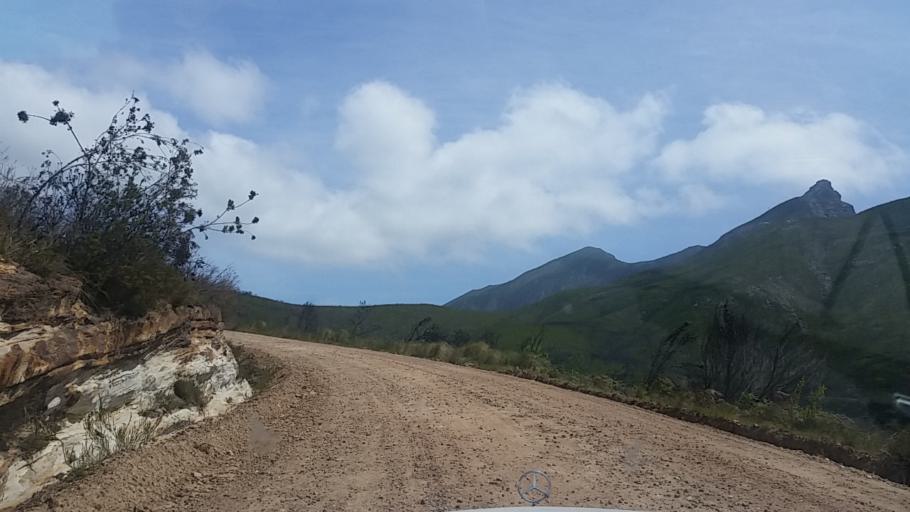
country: ZA
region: Western Cape
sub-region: Eden District Municipality
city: George
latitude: -33.8823
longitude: 22.4360
